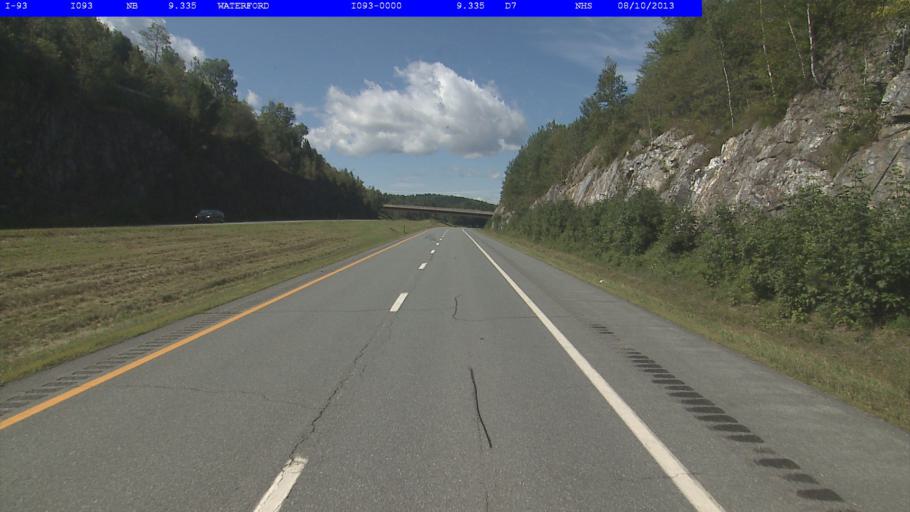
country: US
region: Vermont
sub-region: Caledonia County
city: Saint Johnsbury
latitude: 44.4132
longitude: -71.9867
